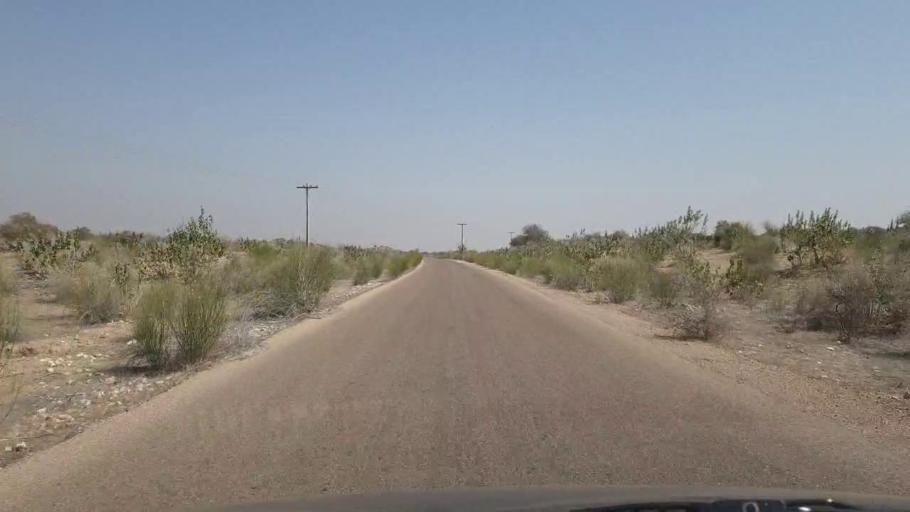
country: PK
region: Sindh
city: Chor
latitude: 25.6194
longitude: 70.0551
